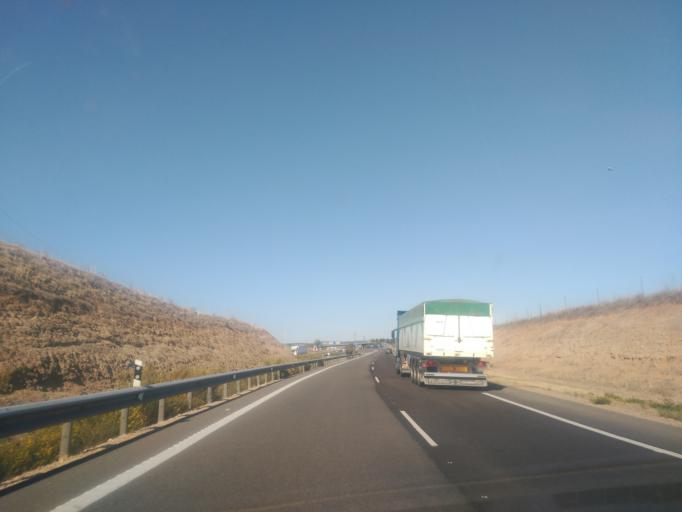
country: ES
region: Castille and Leon
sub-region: Provincia de Valladolid
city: Tordesillas
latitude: 41.5073
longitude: -4.9860
